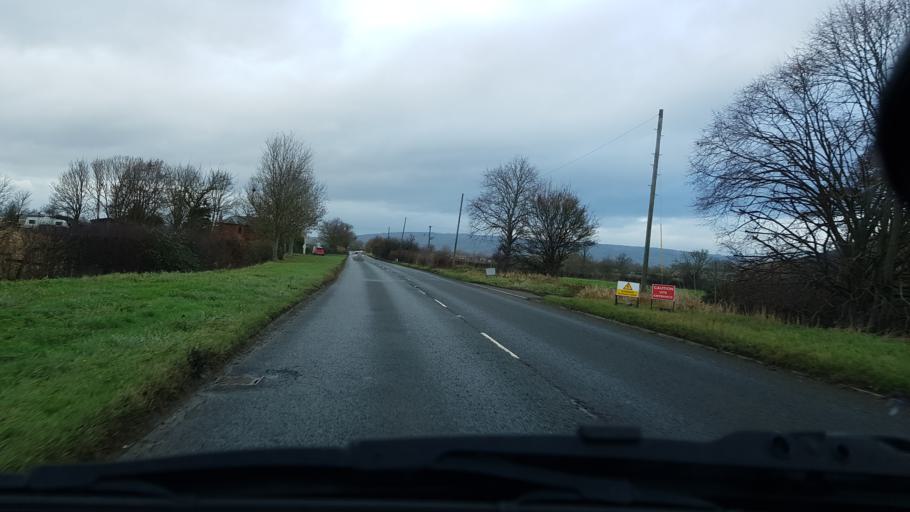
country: GB
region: England
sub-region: Gloucestershire
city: Gotherington
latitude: 51.9729
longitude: -2.0708
